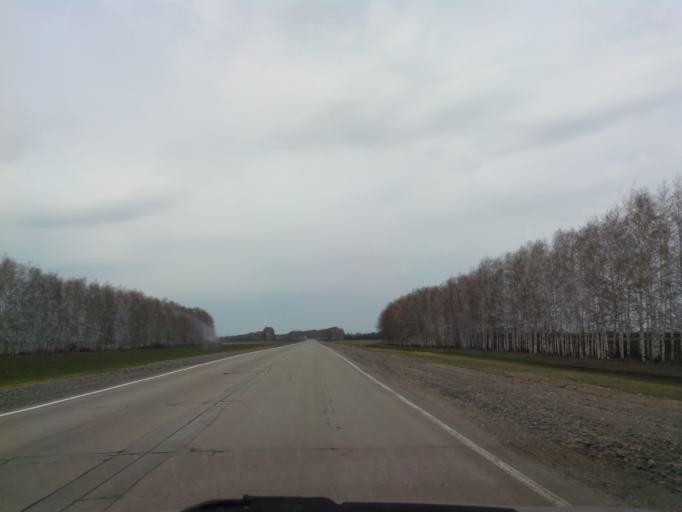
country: RU
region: Tambov
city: Znamenka
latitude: 52.2398
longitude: 41.5316
